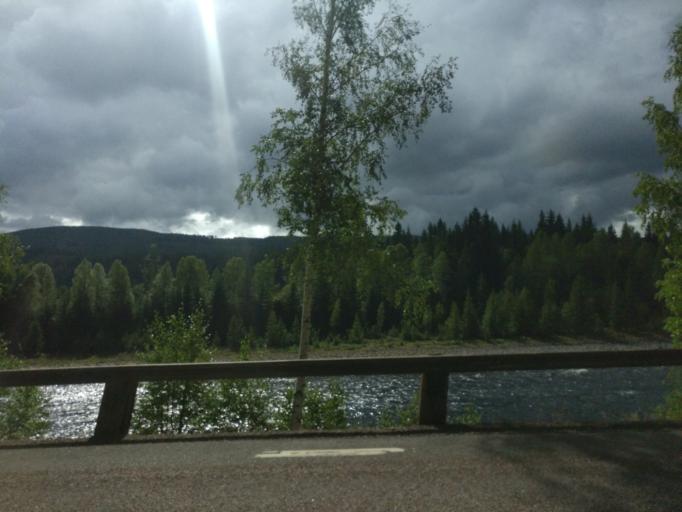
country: SE
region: Vaermland
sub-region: Torsby Kommun
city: Torsby
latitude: 60.7497
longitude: 12.8091
